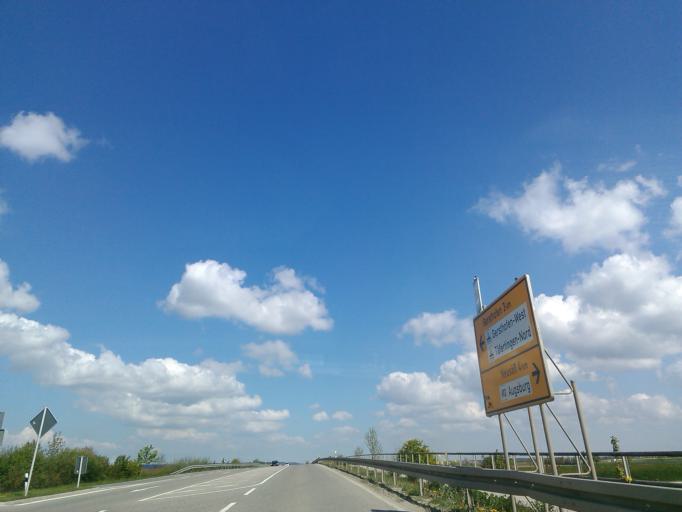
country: DE
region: Bavaria
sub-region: Swabia
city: Gersthofen
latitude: 48.4156
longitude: 10.8389
